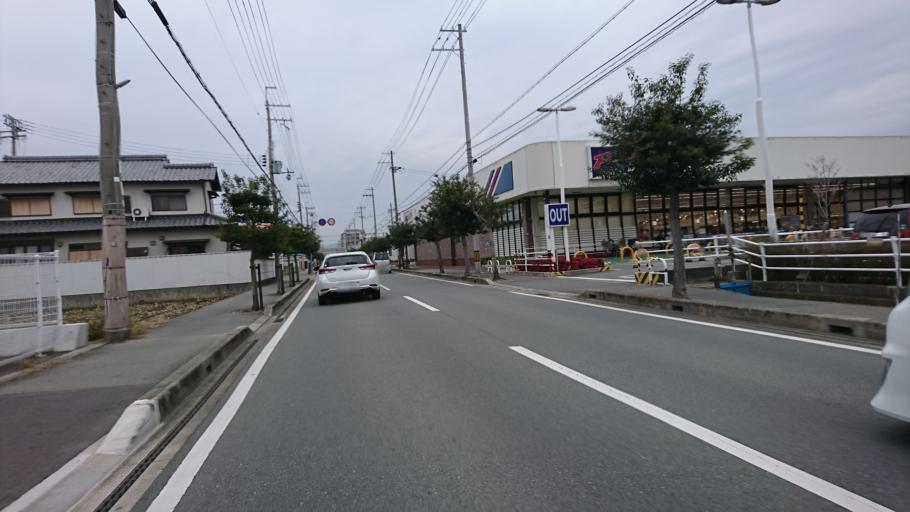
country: JP
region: Hyogo
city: Kakogawacho-honmachi
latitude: 34.7640
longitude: 134.8297
